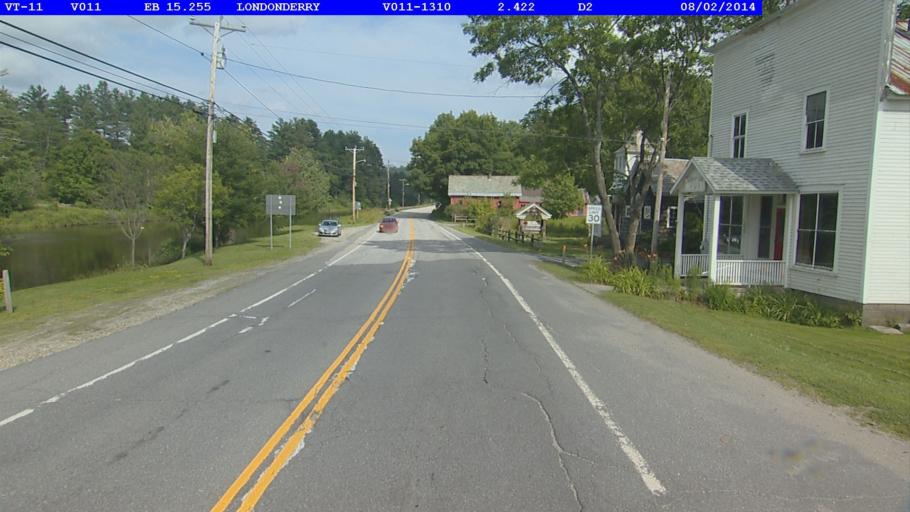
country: US
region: Vermont
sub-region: Windsor County
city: Chester
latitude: 43.2264
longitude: -72.8064
